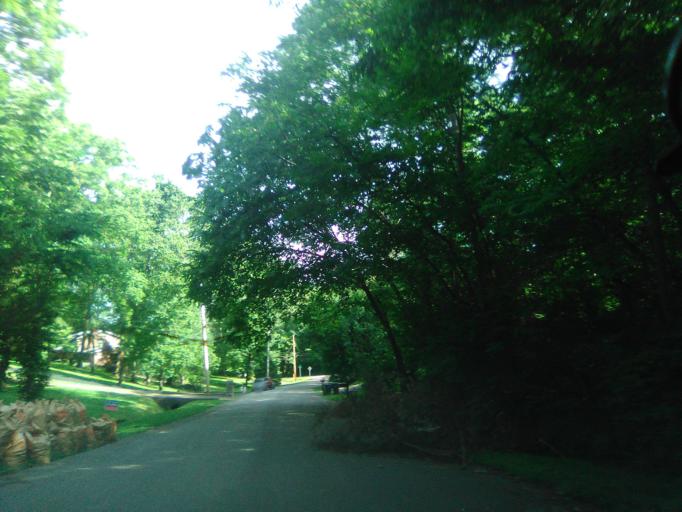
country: US
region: Tennessee
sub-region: Davidson County
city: Belle Meade
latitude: 36.1102
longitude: -86.9049
